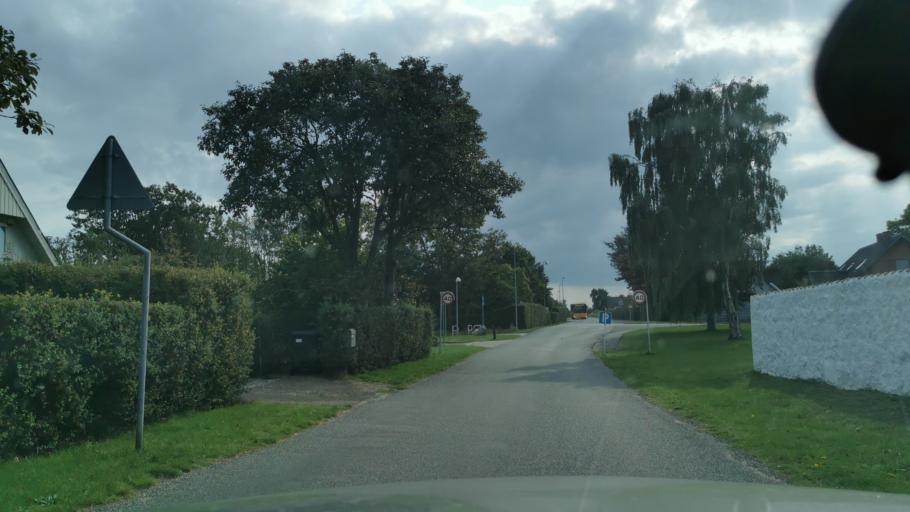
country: DK
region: Zealand
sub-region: Kalundborg Kommune
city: Kalundborg
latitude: 55.6975
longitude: 11.0668
